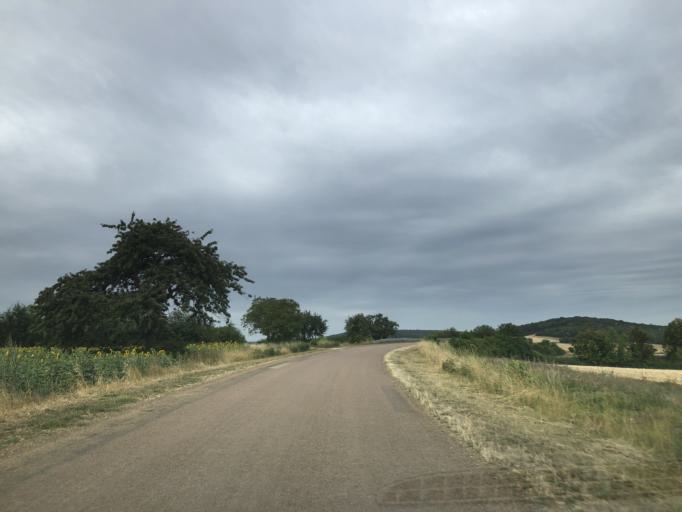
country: FR
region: Bourgogne
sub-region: Departement de l'Yonne
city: Aillant-sur-Tholon
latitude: 47.9082
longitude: 3.3423
